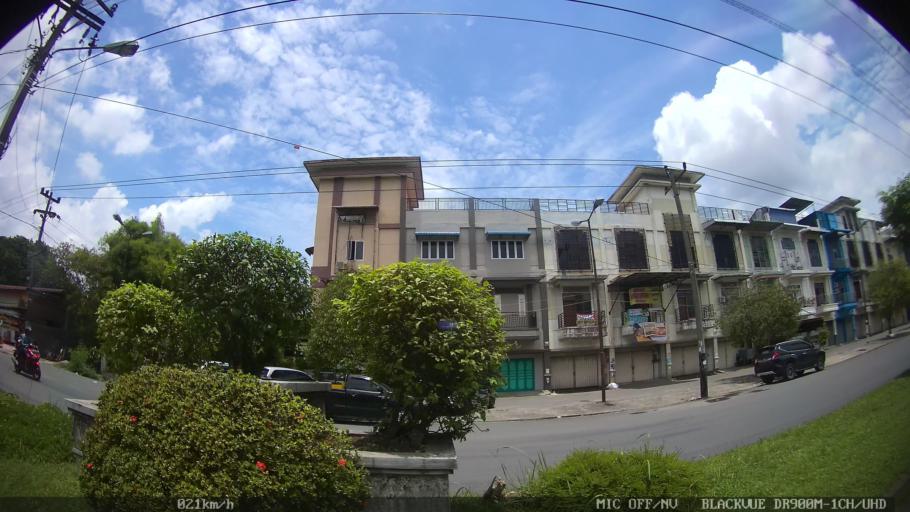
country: ID
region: North Sumatra
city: Medan
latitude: 3.6144
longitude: 98.7124
